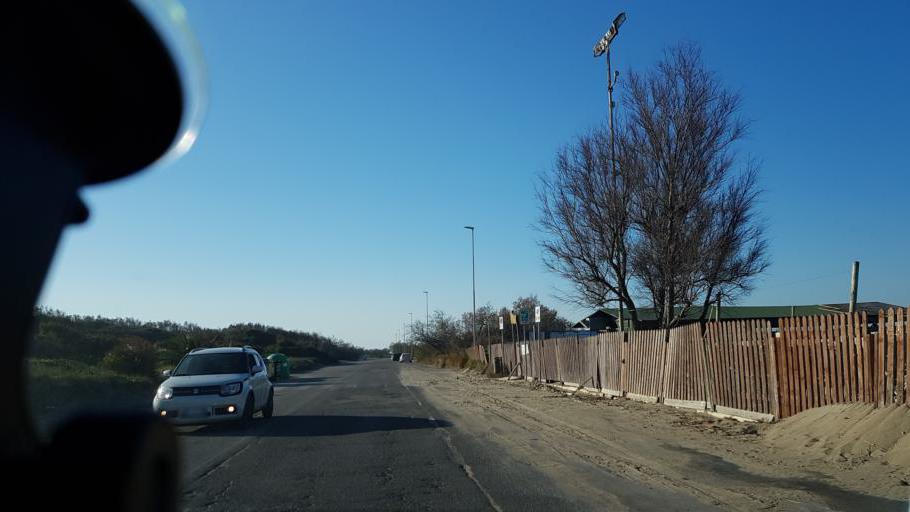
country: IT
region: Apulia
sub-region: Provincia di Lecce
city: Struda
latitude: 40.3930
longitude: 18.3024
